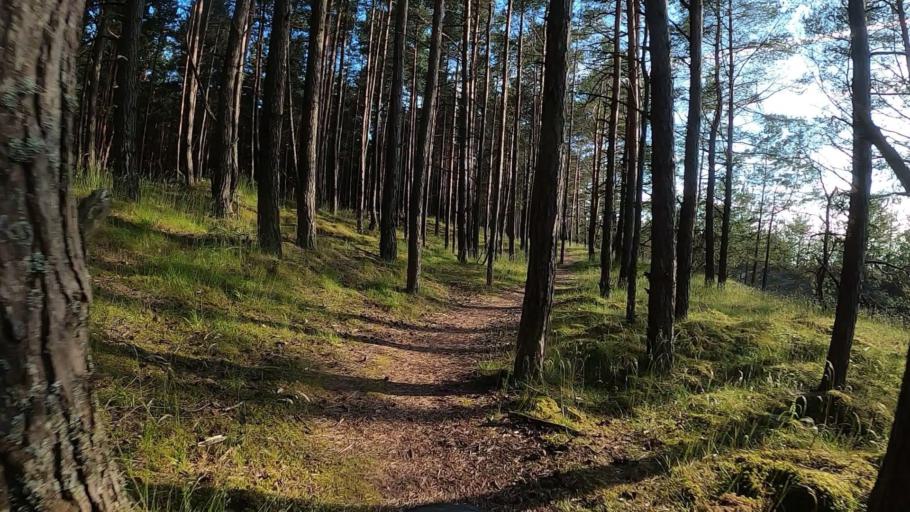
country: LV
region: Carnikava
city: Carnikava
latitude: 57.1221
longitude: 24.2080
